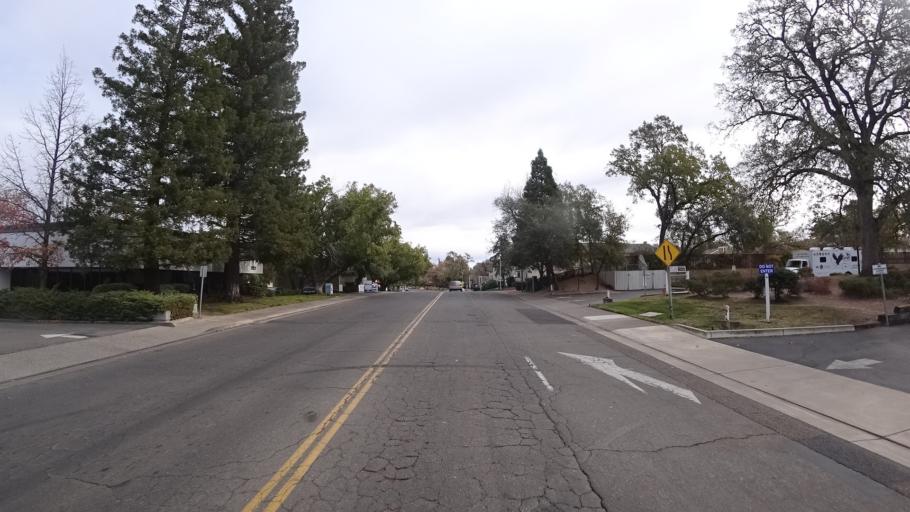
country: US
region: California
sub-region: Sacramento County
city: Fair Oaks
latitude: 38.6697
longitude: -121.2708
